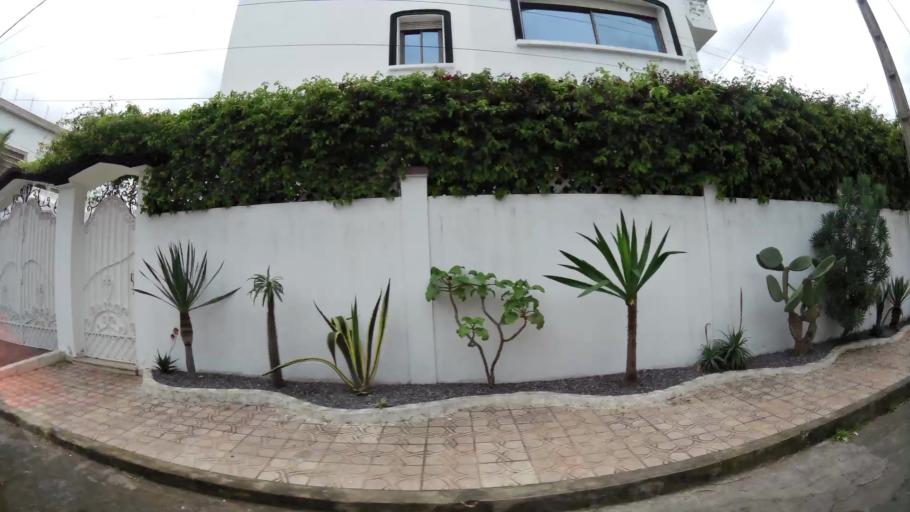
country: MA
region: Grand Casablanca
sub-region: Casablanca
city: Casablanca
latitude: 33.5565
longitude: -7.6208
